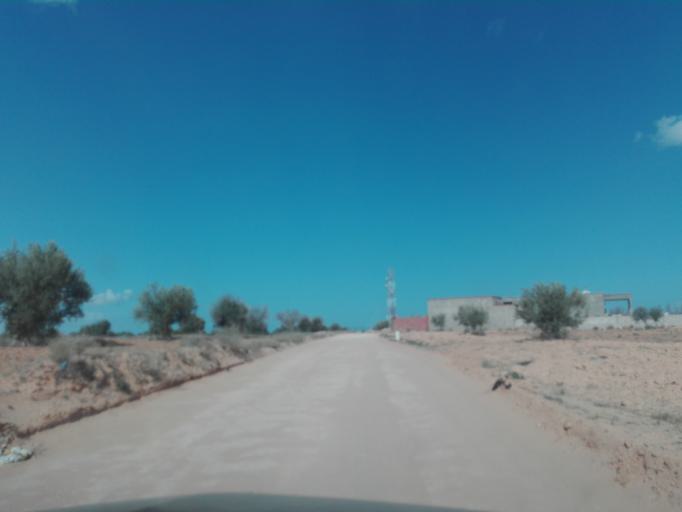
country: TN
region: Madanin
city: Bin Qirdan
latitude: 33.1656
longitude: 11.1962
